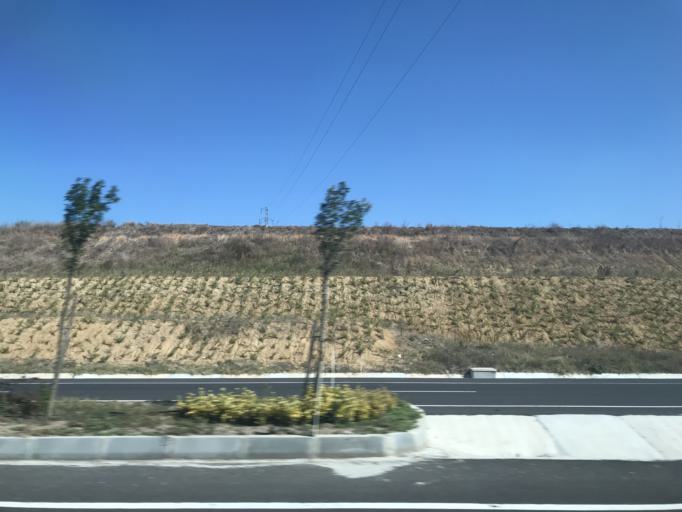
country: TR
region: Tekirdag
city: Muratli
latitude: 41.2080
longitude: 27.5352
